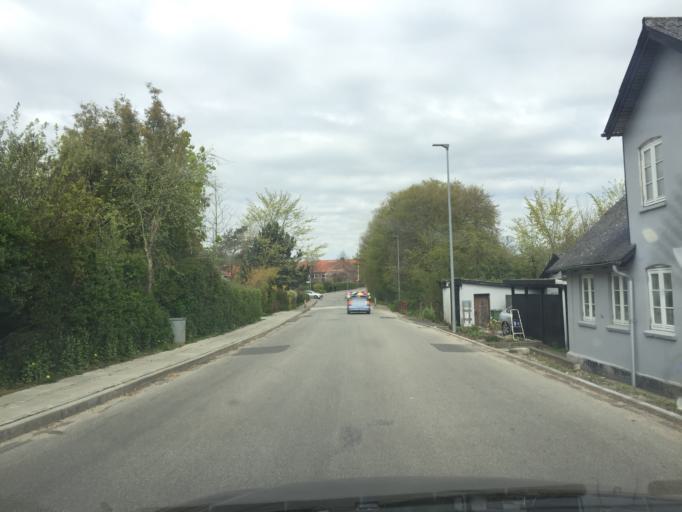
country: DK
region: South Denmark
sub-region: Kolding Kommune
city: Sonder Bjert
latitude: 55.4581
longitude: 9.5571
